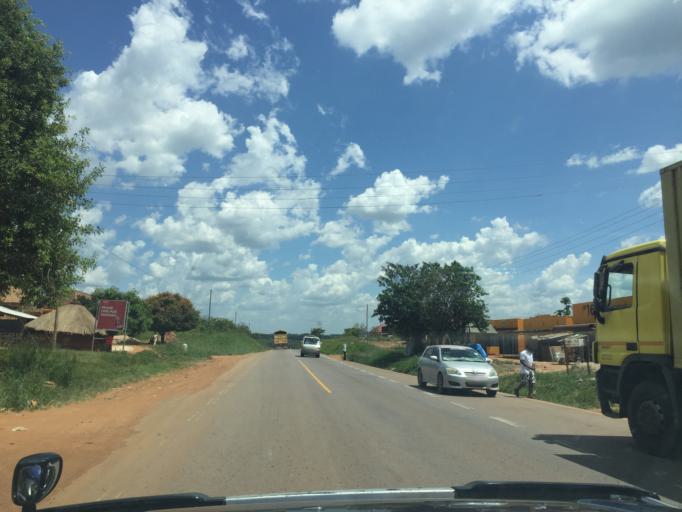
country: UG
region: Central Region
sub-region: Nakasongola District
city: Nakasongola
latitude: 1.3582
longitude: 32.3716
